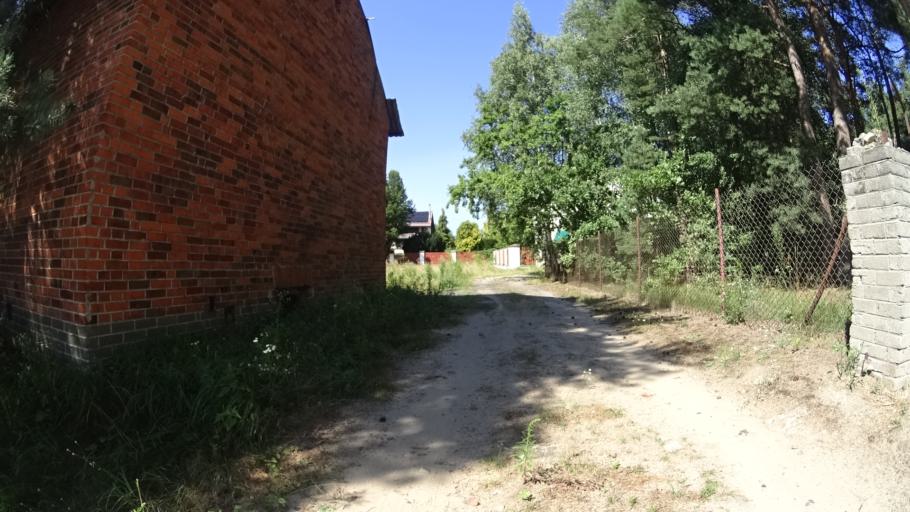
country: PL
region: Masovian Voivodeship
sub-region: Powiat bialobrzeski
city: Bialobrzegi
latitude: 51.6676
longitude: 20.9212
